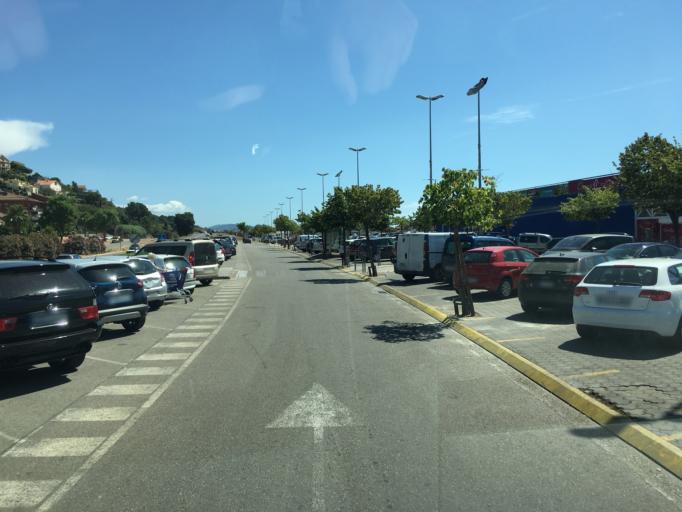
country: ES
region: Catalonia
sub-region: Provincia de Barcelona
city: Santa Susanna
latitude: 41.6372
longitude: 2.7166
